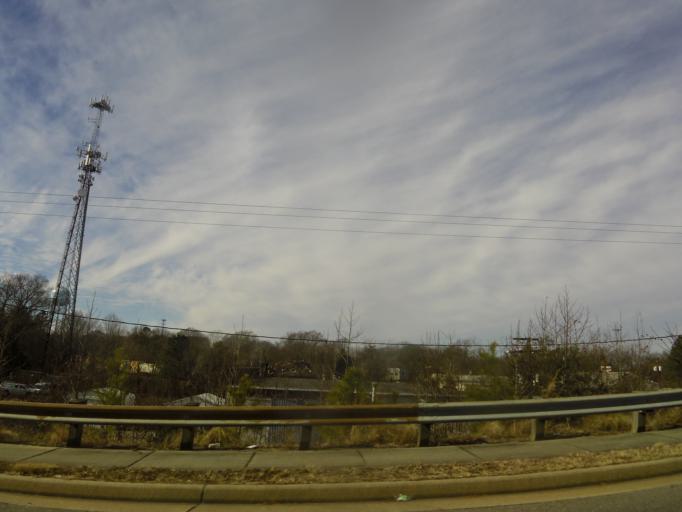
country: US
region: Virginia
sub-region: City of Hopewell
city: Hopewell
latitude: 37.2982
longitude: -77.2903
